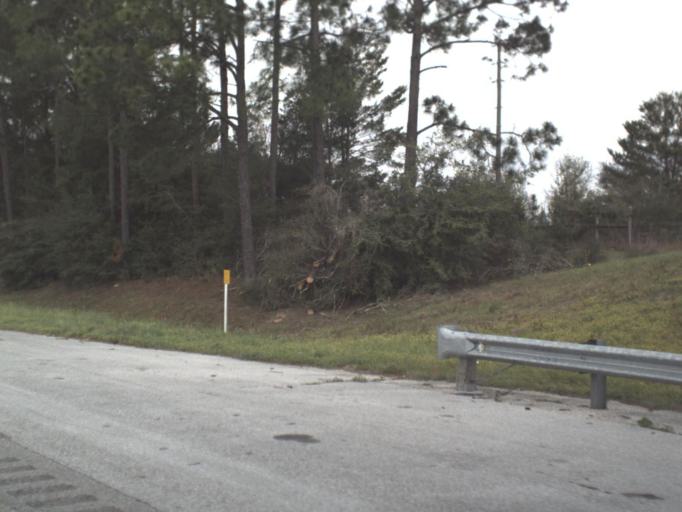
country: US
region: Florida
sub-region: Okaloosa County
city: Crestview
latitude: 30.7185
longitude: -86.4544
